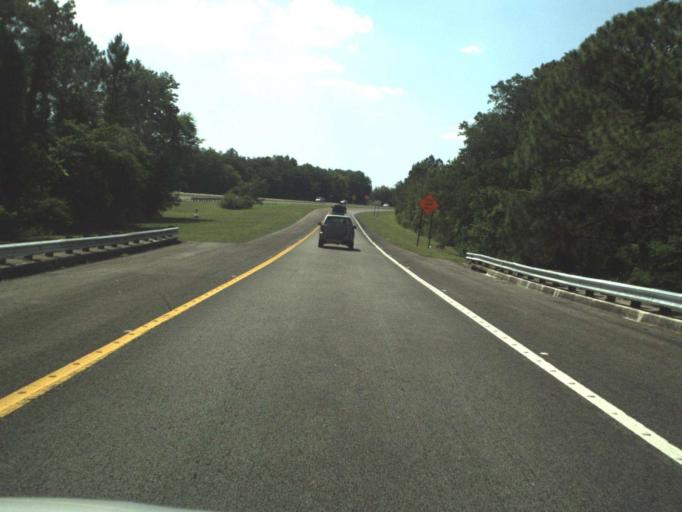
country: US
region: Florida
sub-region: Orange County
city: Bithlo
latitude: 28.5387
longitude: -81.0808
